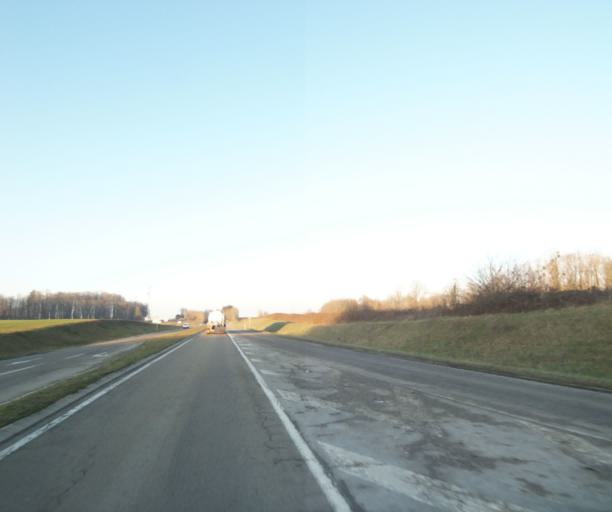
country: FR
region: Champagne-Ardenne
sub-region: Departement de la Haute-Marne
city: Bienville
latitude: 48.5717
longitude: 5.0352
